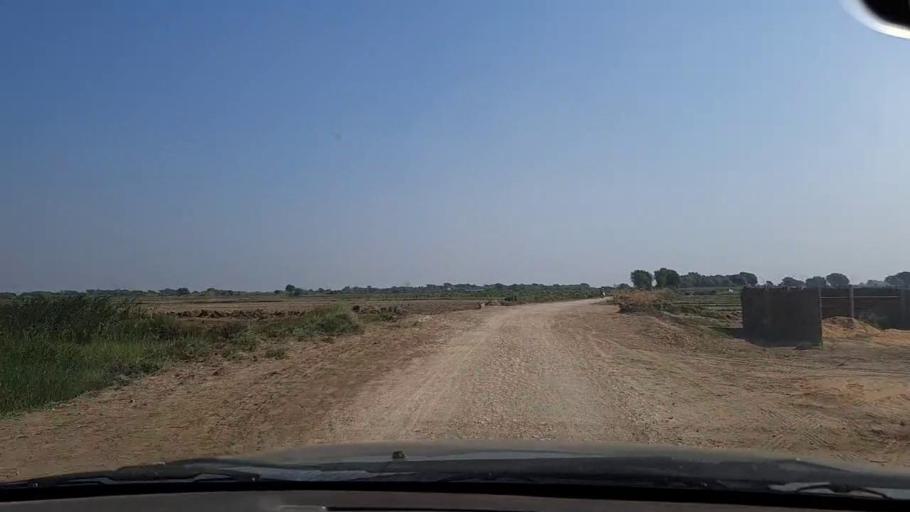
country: PK
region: Sindh
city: Chuhar Jamali
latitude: 24.4191
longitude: 67.8273
